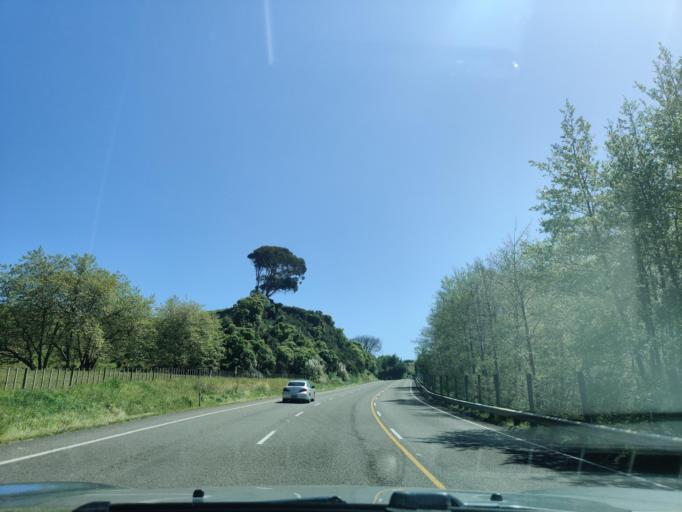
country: NZ
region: Manawatu-Wanganui
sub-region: Wanganui District
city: Wanganui
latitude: -39.8406
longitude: 174.9189
